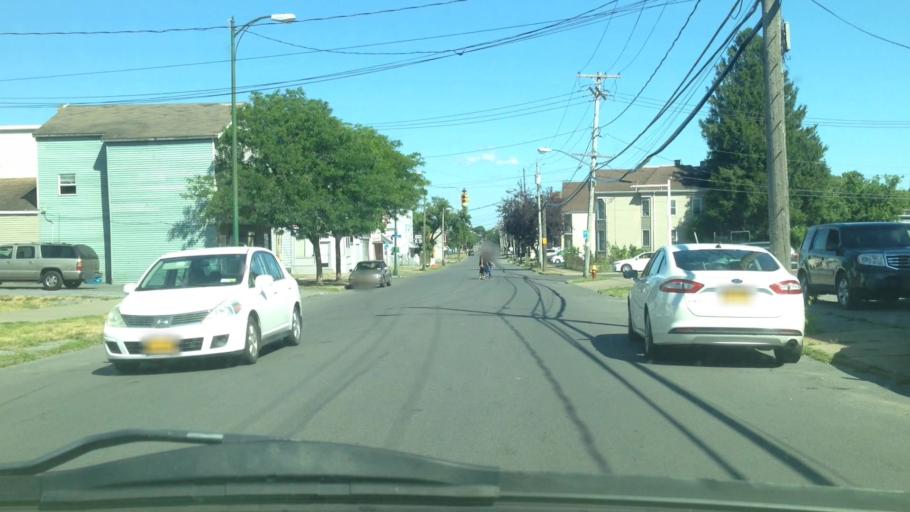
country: US
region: New York
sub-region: Oneida County
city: Utica
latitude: 43.0965
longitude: -75.2120
